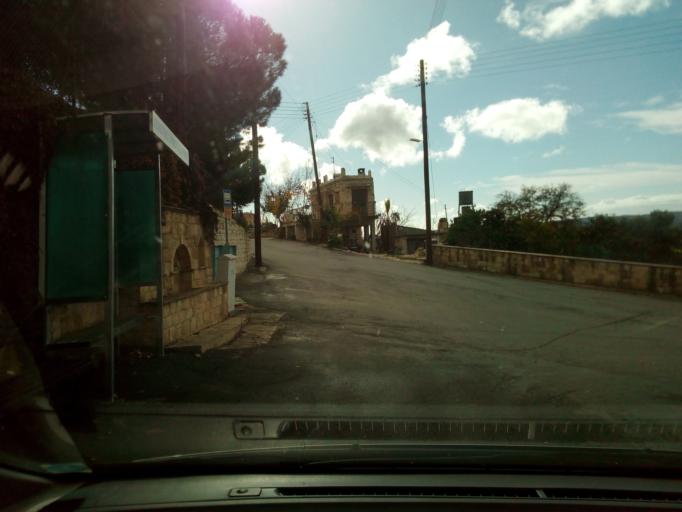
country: CY
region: Pafos
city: Tala
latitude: 34.9251
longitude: 32.5139
